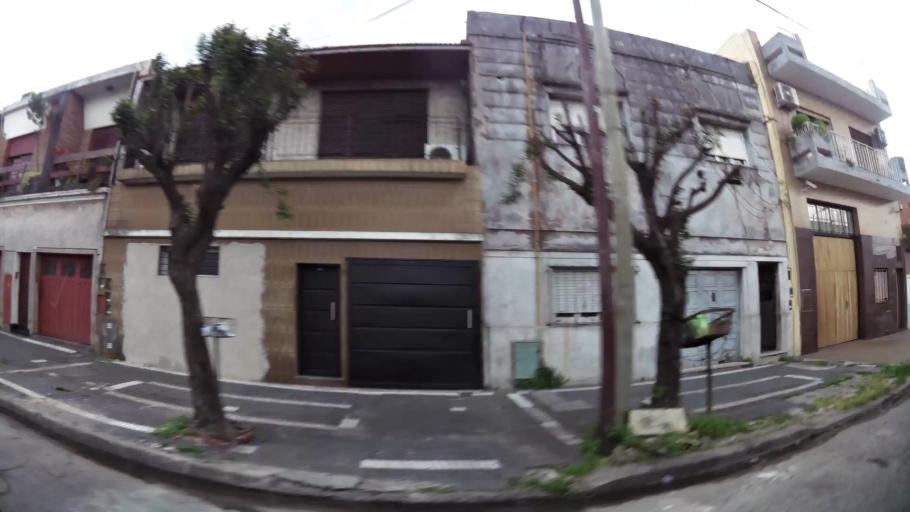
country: AR
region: Buenos Aires
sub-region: Partido de Lanus
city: Lanus
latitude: -34.6815
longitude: -58.3894
